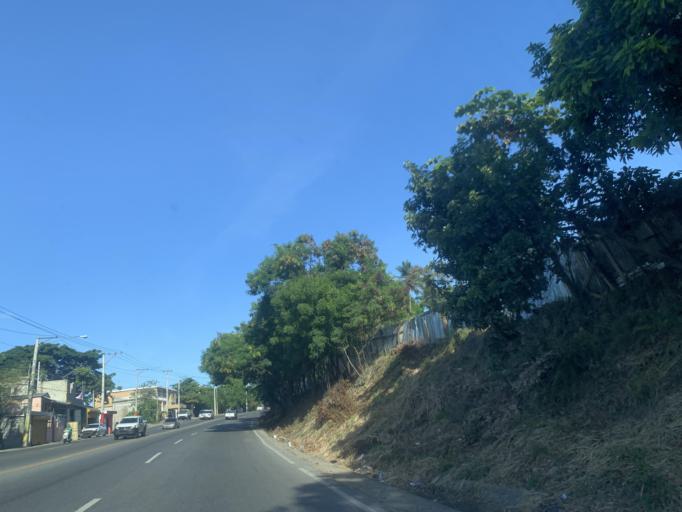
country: DO
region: San Cristobal
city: El Carril
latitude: 18.4358
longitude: -70.0141
